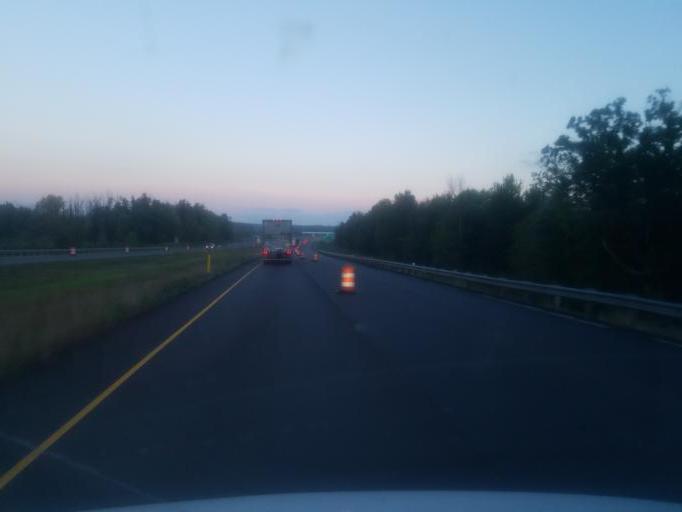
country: US
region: Ohio
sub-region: Ashtabula County
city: Jefferson
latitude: 41.8027
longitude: -80.7515
